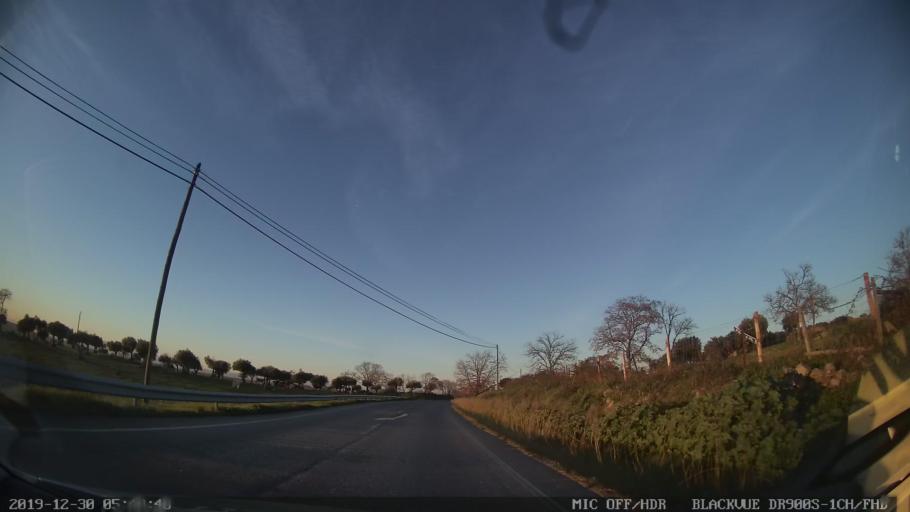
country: PT
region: Castelo Branco
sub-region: Idanha-A-Nova
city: Idanha-a-Nova
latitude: 39.9777
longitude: -7.2423
